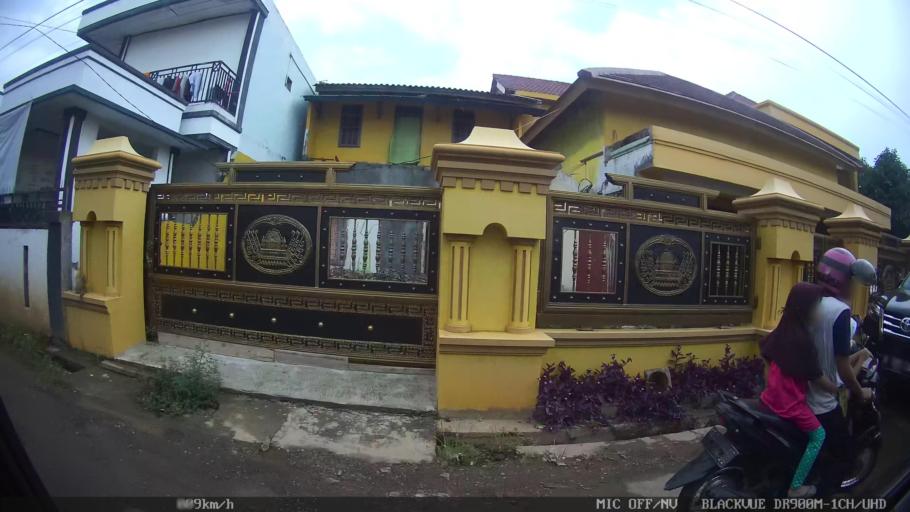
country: ID
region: Lampung
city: Kedaton
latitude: -5.3828
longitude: 105.2541
